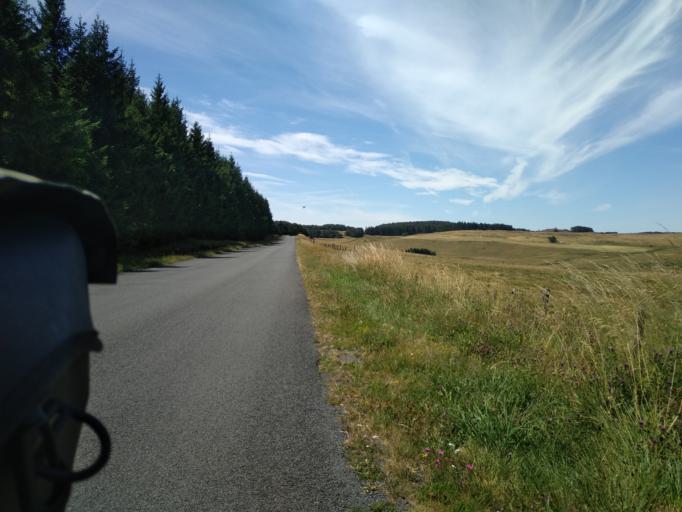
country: FR
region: Midi-Pyrenees
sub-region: Departement de l'Aveyron
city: Laguiole
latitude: 44.6665
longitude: 2.9613
